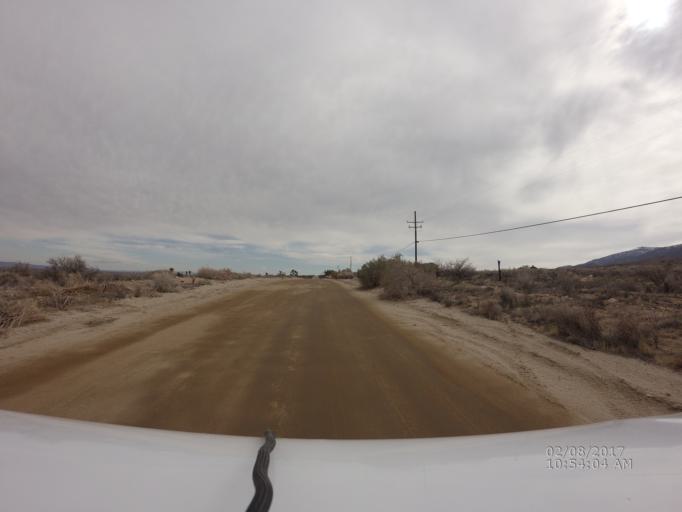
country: US
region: California
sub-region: San Bernardino County
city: Pinon Hills
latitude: 34.4694
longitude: -117.7265
